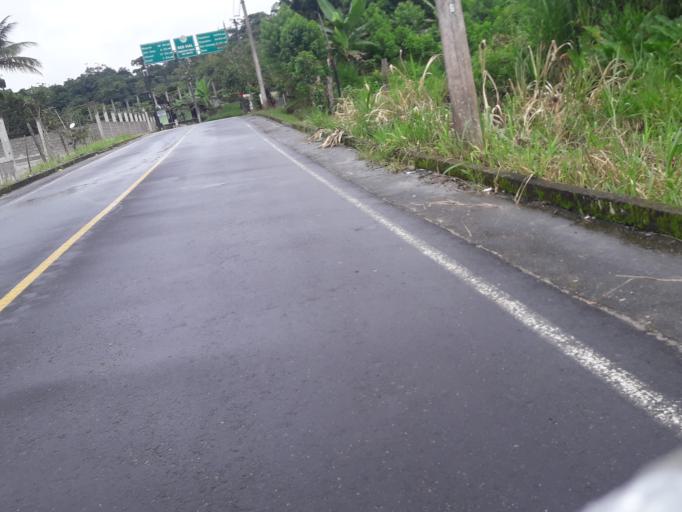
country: EC
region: Napo
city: Tena
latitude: -0.9675
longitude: -77.8552
